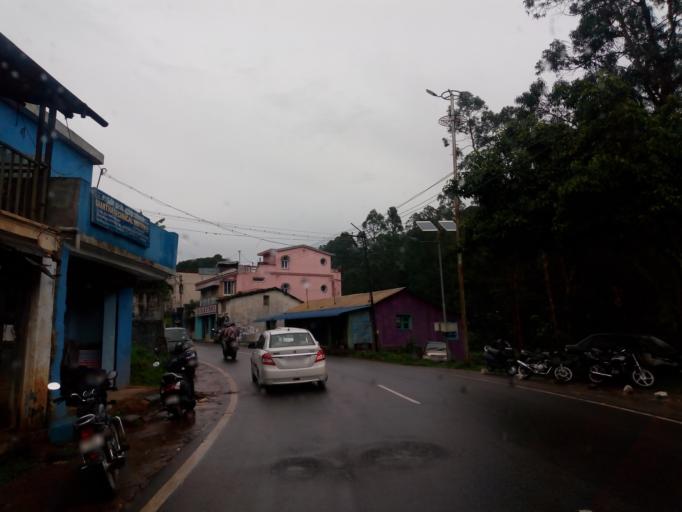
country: IN
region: Tamil Nadu
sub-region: Nilgiri
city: Wellington
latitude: 11.3570
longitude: 76.7842
